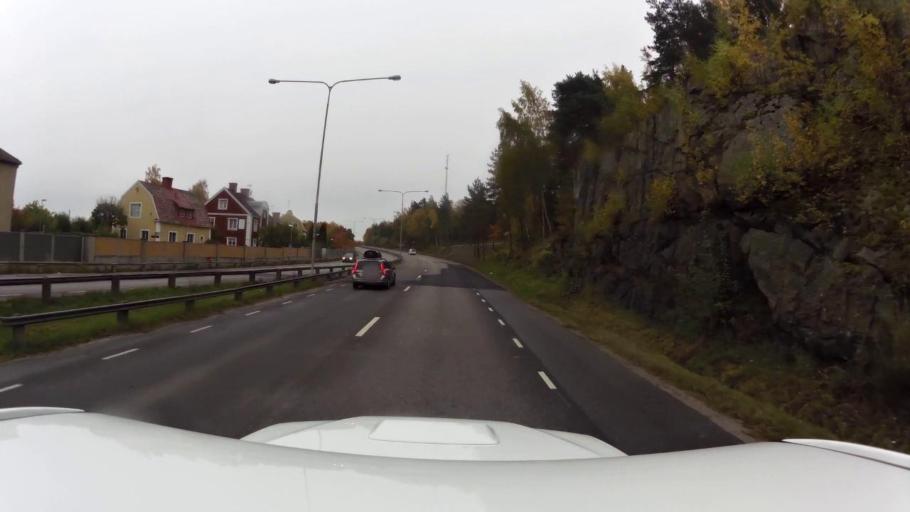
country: SE
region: OEstergoetland
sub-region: Linkopings Kommun
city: Linkoping
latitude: 58.4007
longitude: 15.6384
